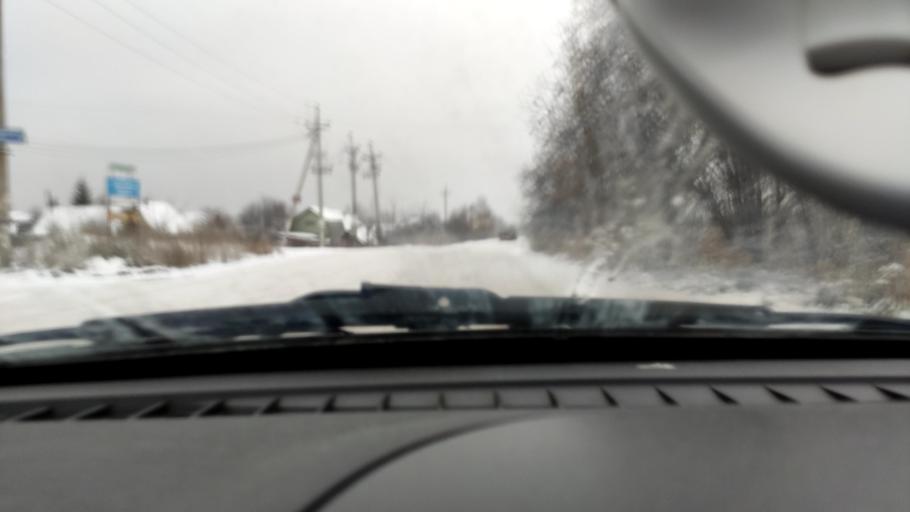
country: RU
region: Perm
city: Polazna
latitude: 58.1769
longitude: 56.4067
